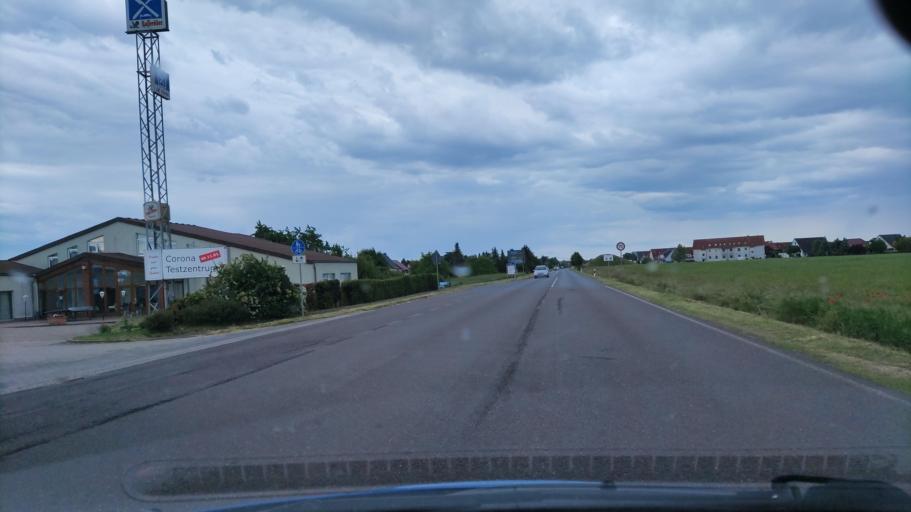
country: DE
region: Saxony-Anhalt
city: Wolmirstedt
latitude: 52.2625
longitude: 11.6323
